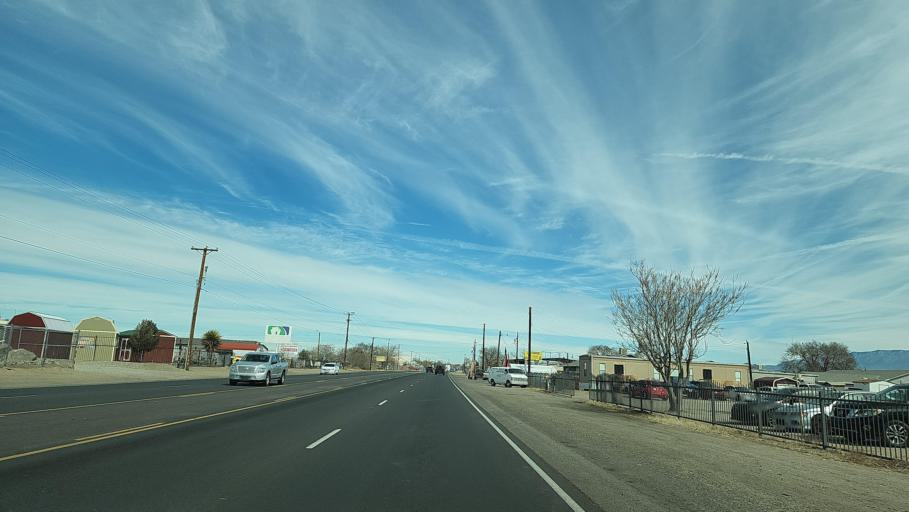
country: US
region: New Mexico
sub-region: Bernalillo County
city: South Valley
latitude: 35.0411
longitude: -106.7110
